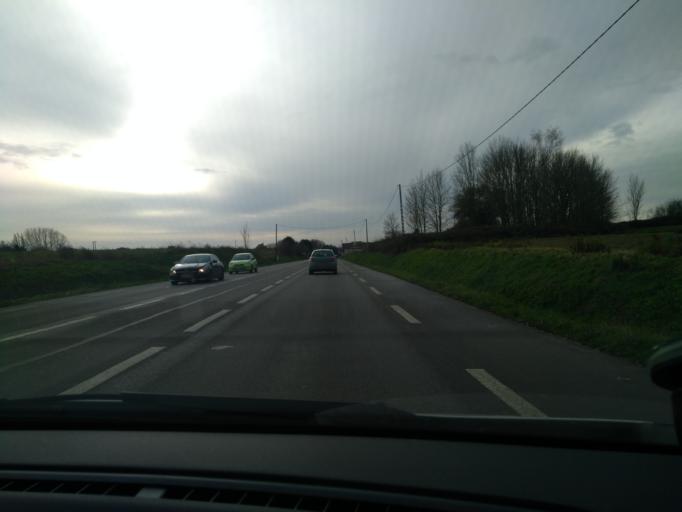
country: FR
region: Nord-Pas-de-Calais
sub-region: Departement du Nord
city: Maubeuge
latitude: 50.3179
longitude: 3.9767
